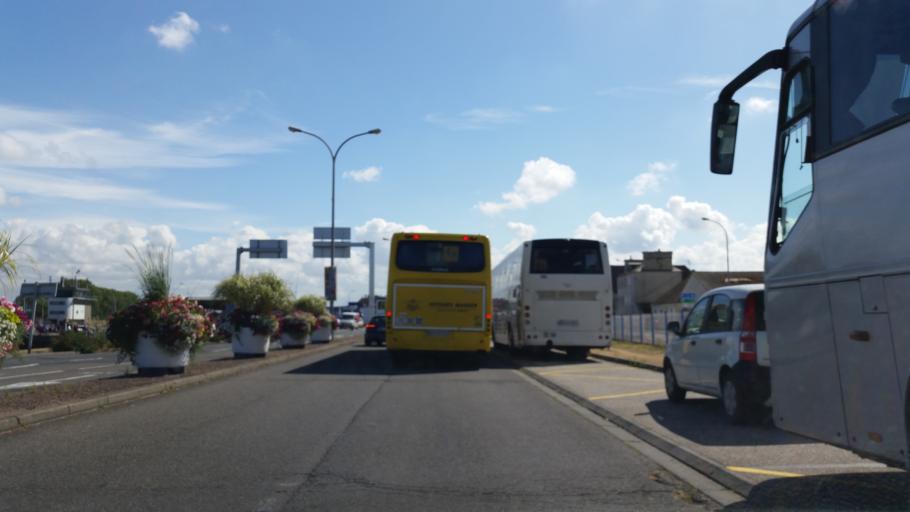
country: FR
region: Lower Normandy
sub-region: Departement du Calvados
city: Ouistreham
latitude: 49.2817
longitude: -0.2498
